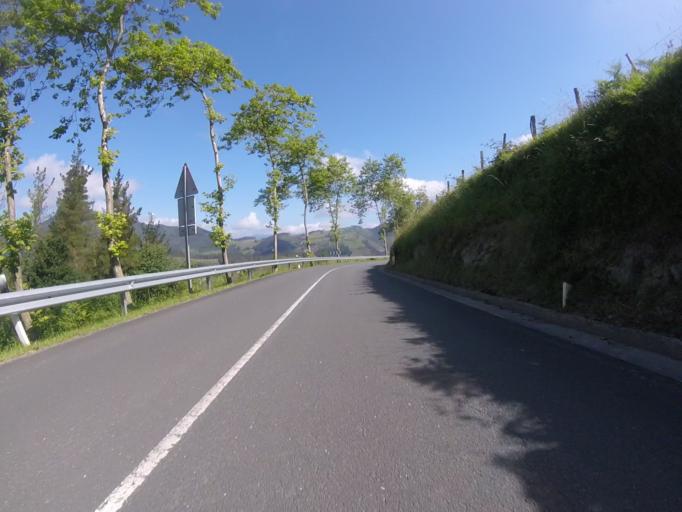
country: ES
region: Basque Country
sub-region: Provincia de Guipuzcoa
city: Ormaiztegui
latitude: 43.0893
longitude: -2.2436
